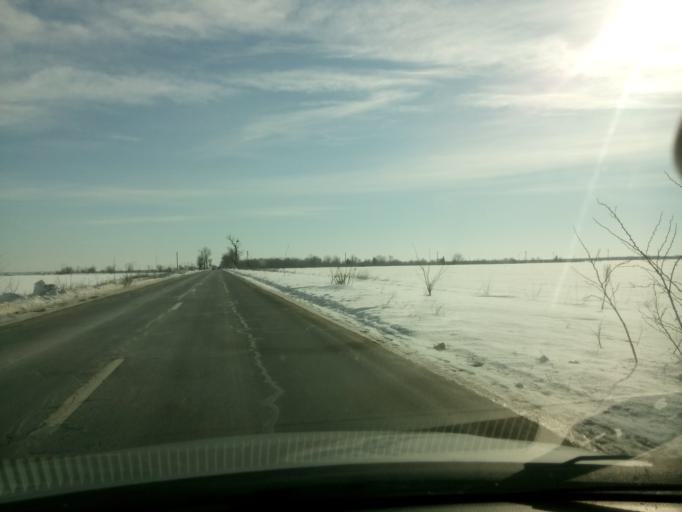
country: RO
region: Ilfov
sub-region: Comuna Glina
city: Glina
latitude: 44.3334
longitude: 26.2468
